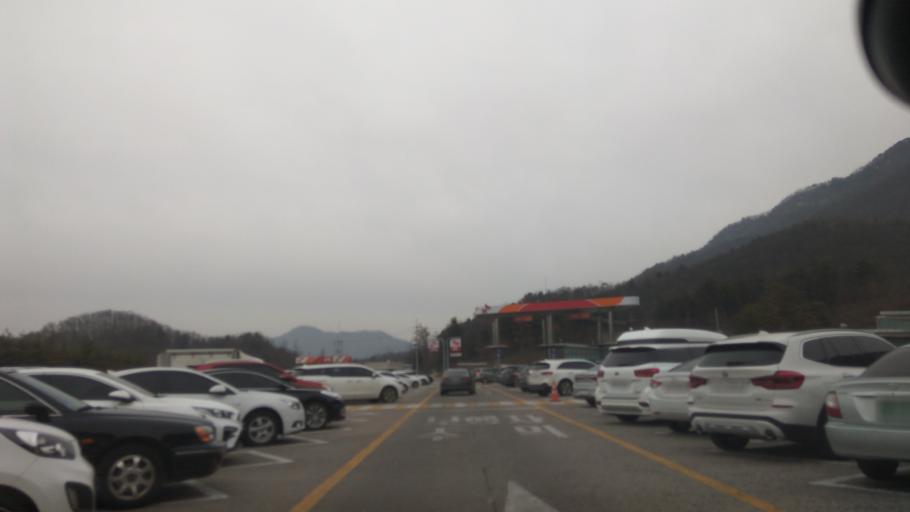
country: KR
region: Gyeonggi-do
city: Cheongpyeong
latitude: 37.7019
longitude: 127.5460
